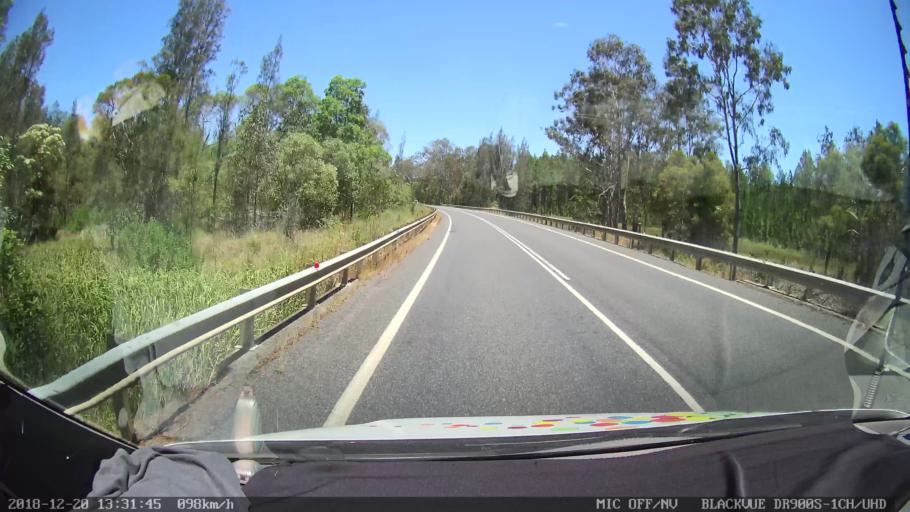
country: AU
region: New South Wales
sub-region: Clarence Valley
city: Gordon
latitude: -29.2223
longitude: 152.9877
